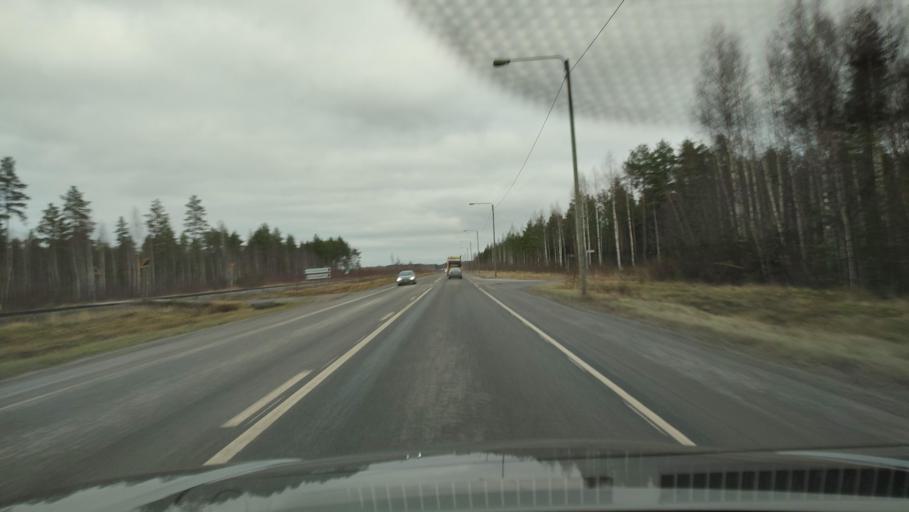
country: FI
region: Southern Ostrobothnia
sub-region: Seinaejoki
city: Ilmajoki
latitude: 62.7474
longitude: 22.6368
